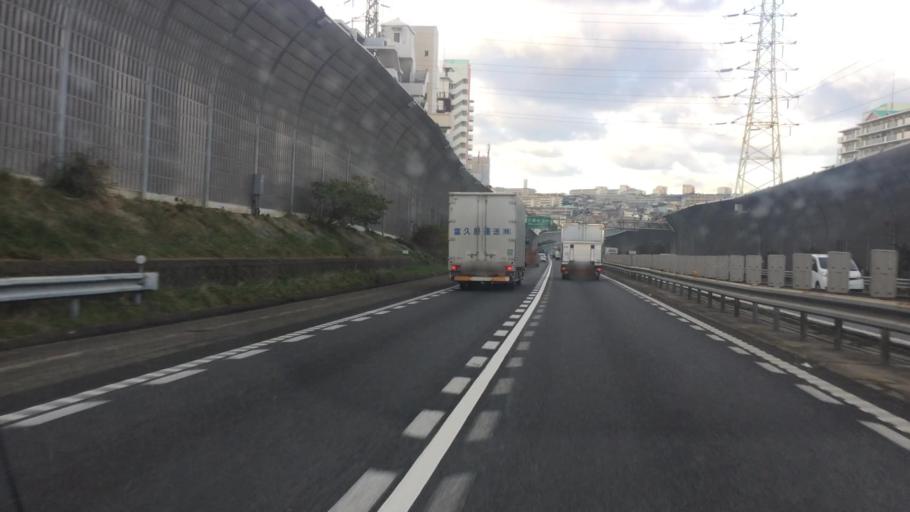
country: JP
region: Hyogo
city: Akashi
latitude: 34.6503
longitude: 135.0441
